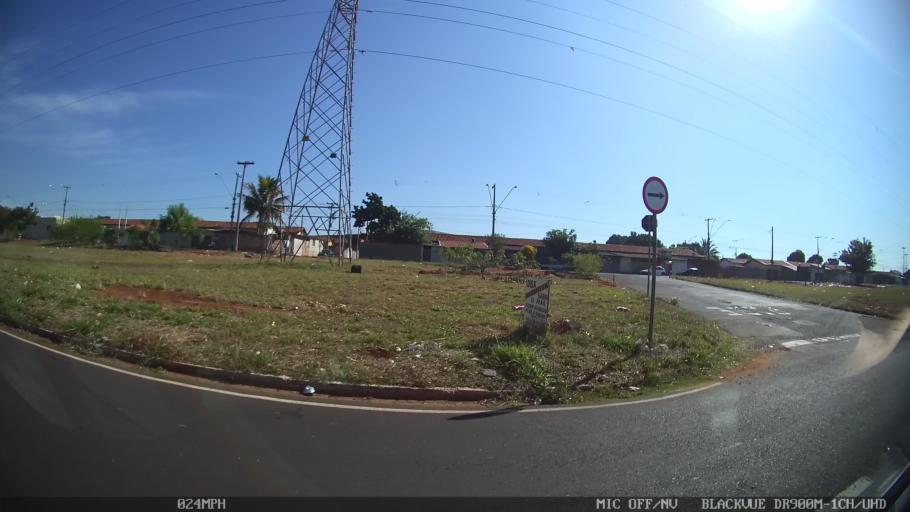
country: BR
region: Sao Paulo
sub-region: Sao Jose Do Rio Preto
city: Sao Jose do Rio Preto
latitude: -20.7665
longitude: -49.3829
